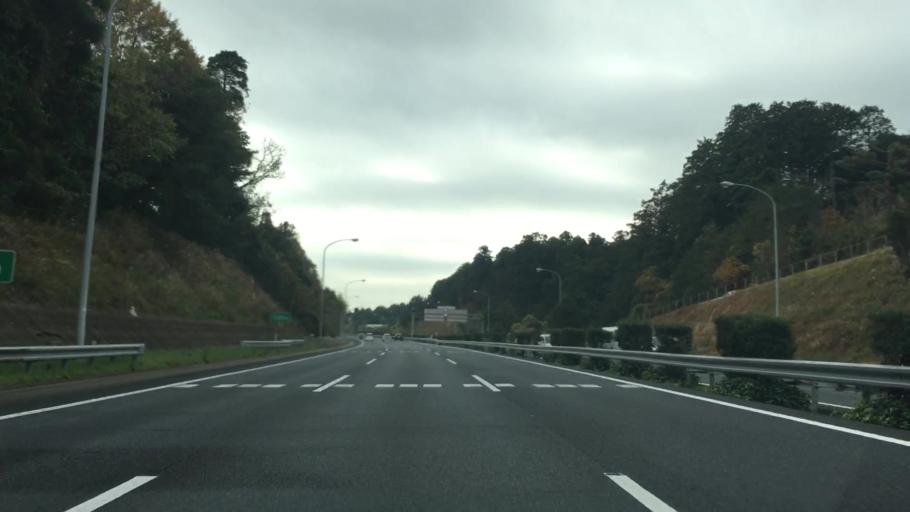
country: JP
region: Chiba
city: Narita
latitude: 35.7615
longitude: 140.3229
